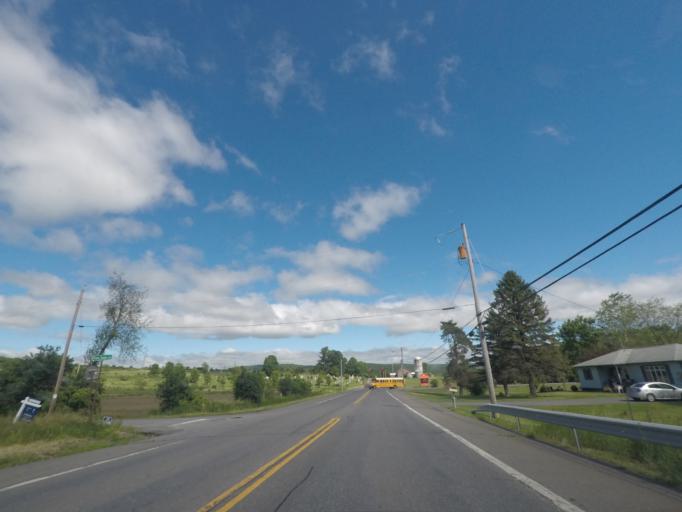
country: US
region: New York
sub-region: Columbia County
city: Philmont
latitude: 42.1762
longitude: -73.5964
